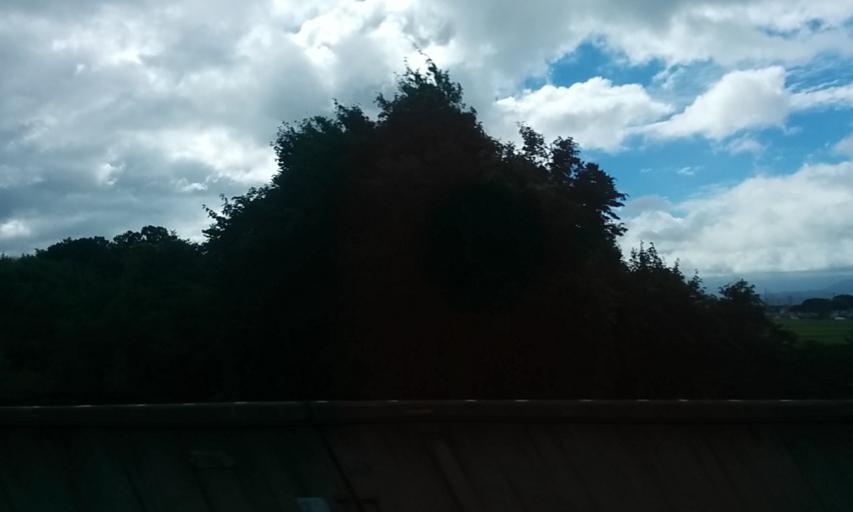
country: JP
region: Fukushima
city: Koriyama
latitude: 37.4376
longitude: 140.4012
